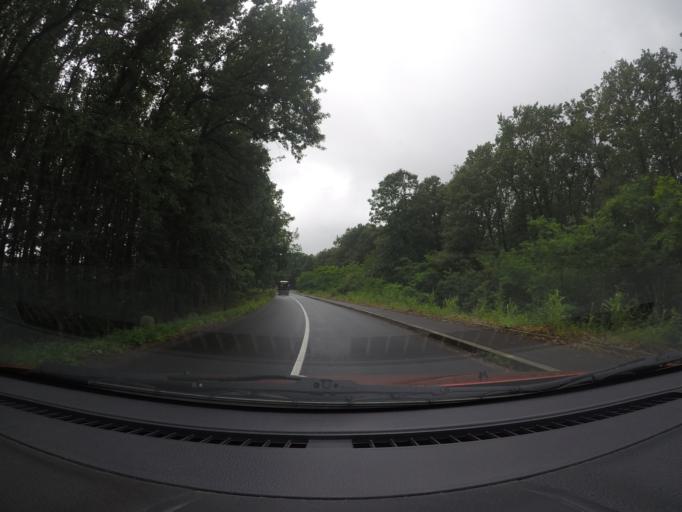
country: RS
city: Rusanj
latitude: 44.6817
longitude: 20.5377
